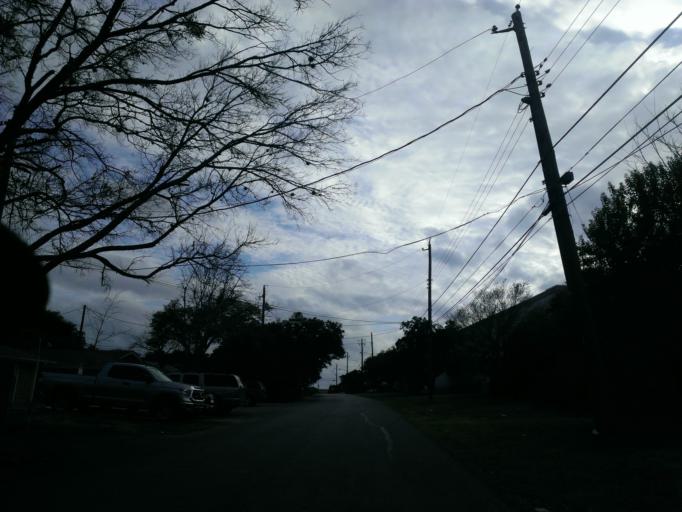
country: US
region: Texas
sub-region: Travis County
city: Wells Branch
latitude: 30.3827
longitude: -97.6842
